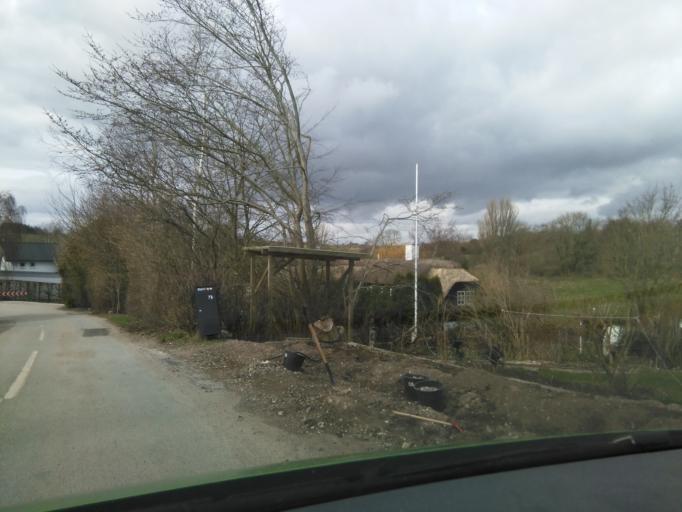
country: DK
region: Central Jutland
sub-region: Arhus Kommune
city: Beder
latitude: 56.0329
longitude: 10.2359
